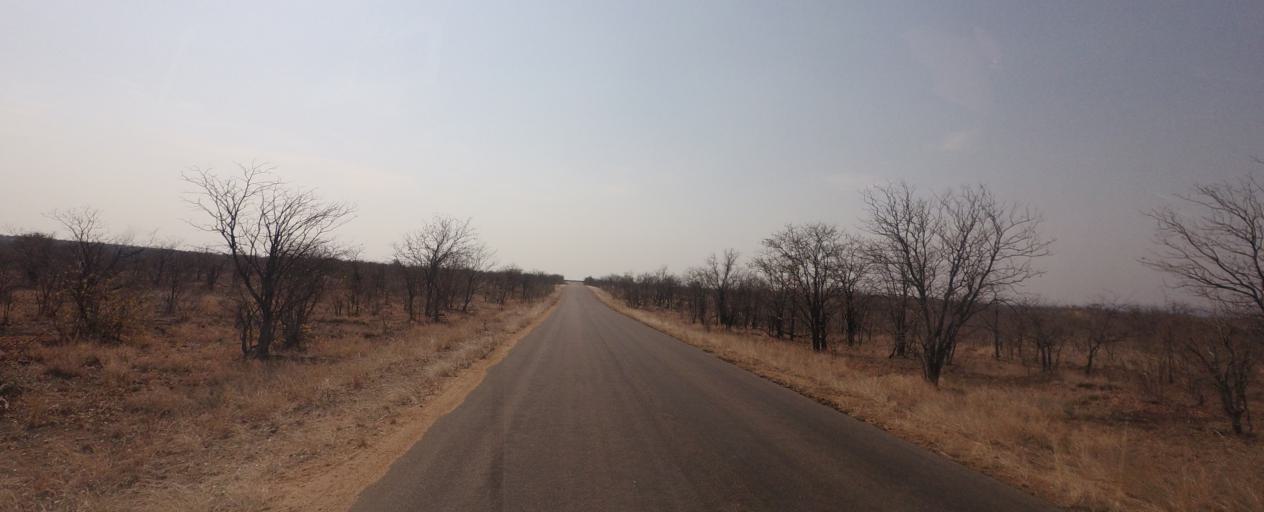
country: ZA
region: Limpopo
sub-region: Mopani District Municipality
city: Phalaborwa
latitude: -23.9524
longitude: 31.6205
